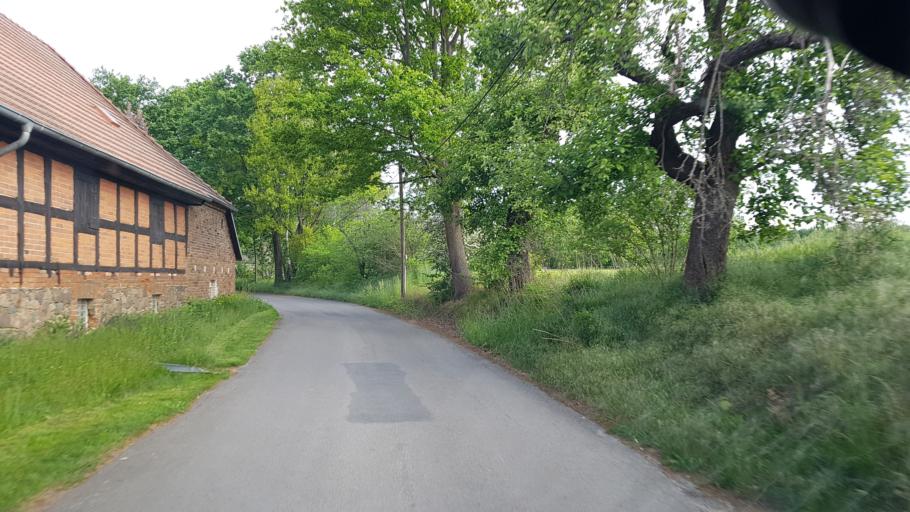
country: DE
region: Brandenburg
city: Luckau
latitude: 51.8084
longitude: 13.6345
